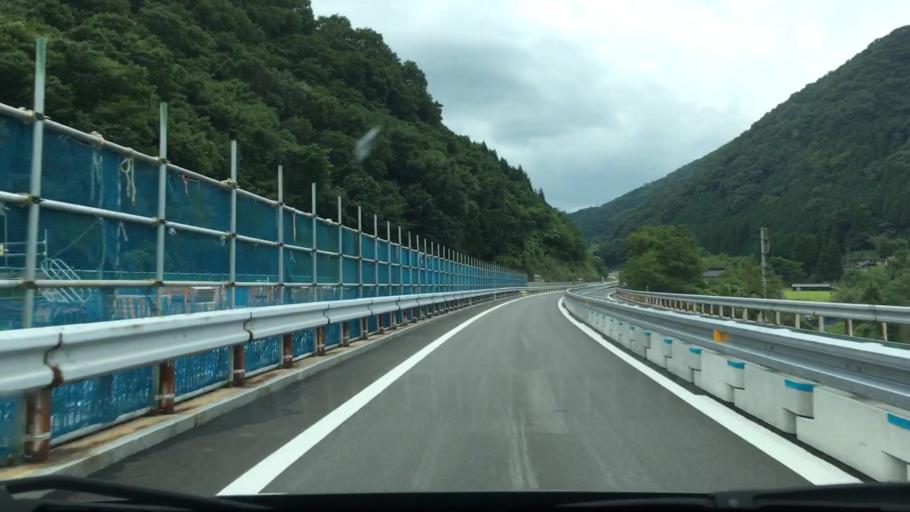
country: JP
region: Okayama
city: Niimi
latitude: 35.0040
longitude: 133.4043
